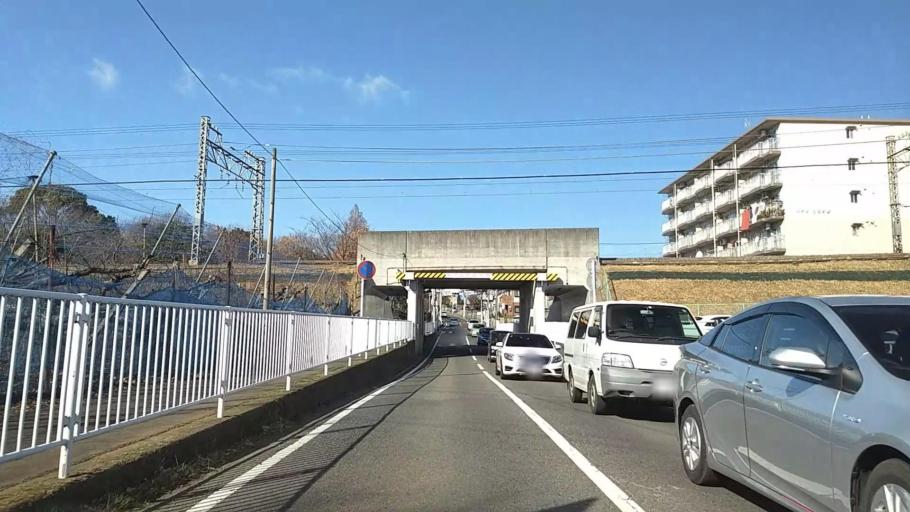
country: JP
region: Kanagawa
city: Isehara
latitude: 35.3936
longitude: 139.3096
